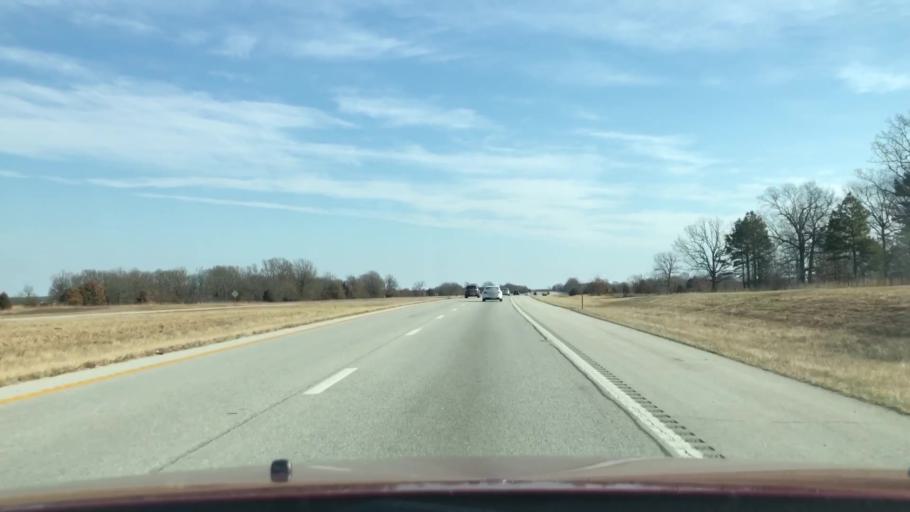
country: US
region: Missouri
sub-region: Webster County
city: Rogersville
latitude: 37.1218
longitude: -93.0008
